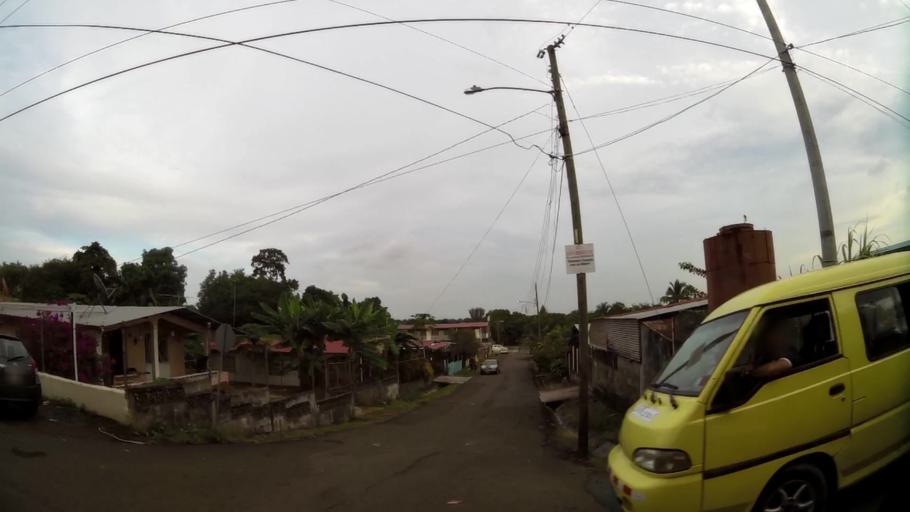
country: PA
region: Panama
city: Tocumen
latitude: 9.0907
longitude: -79.3941
